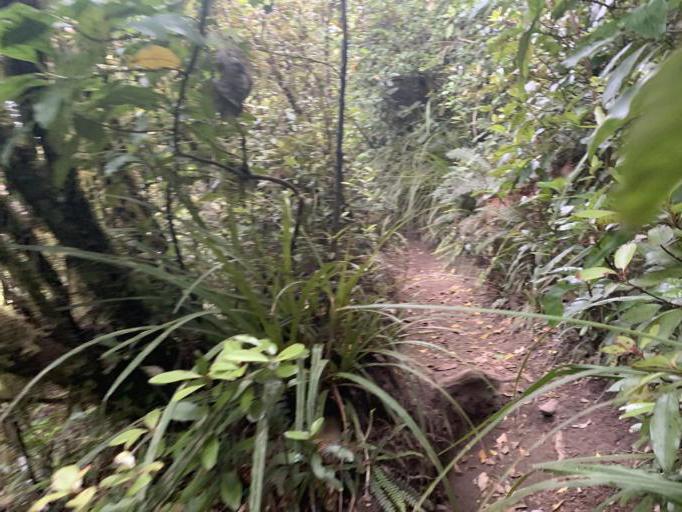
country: NZ
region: Waikato
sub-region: Taupo District
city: Taupo
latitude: -38.6950
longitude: 176.1618
